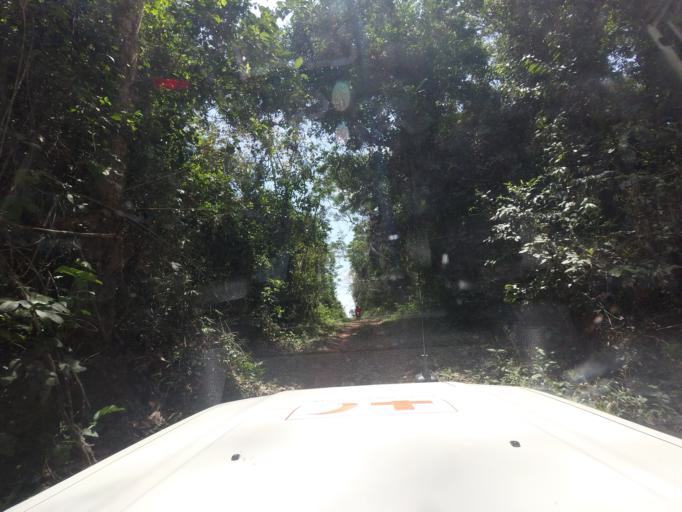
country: GN
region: Nzerekore
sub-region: Yomou
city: Yomou
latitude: 7.3761
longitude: -9.3095
